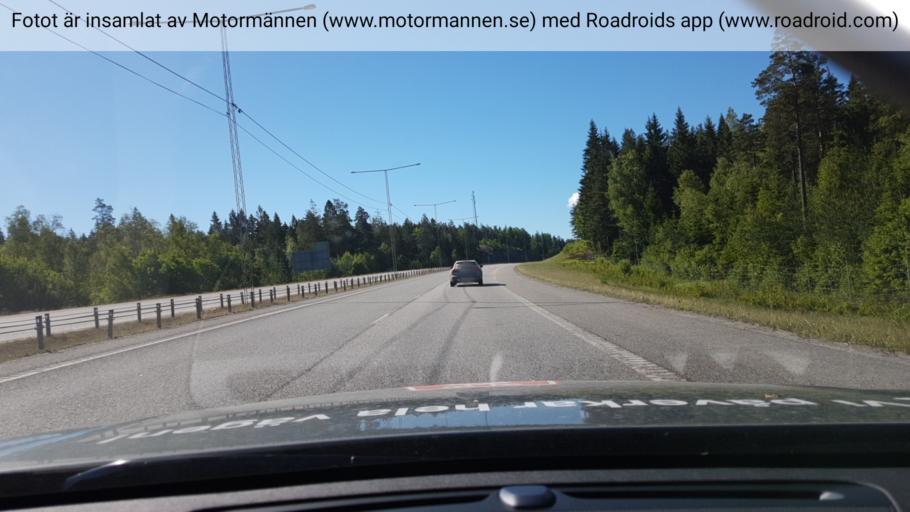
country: SE
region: Stockholm
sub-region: Haninge Kommun
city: Haninge
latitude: 59.1453
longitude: 18.1598
